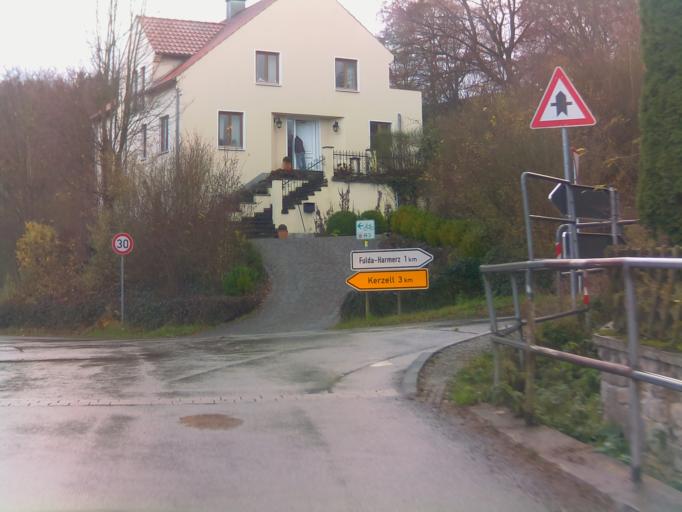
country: DE
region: Hesse
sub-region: Regierungsbezirk Kassel
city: Eichenzell
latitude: 50.5102
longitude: 9.6659
